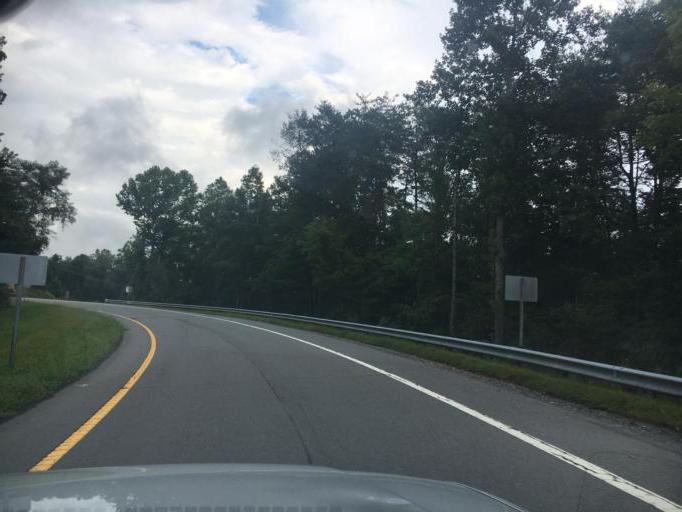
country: US
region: North Carolina
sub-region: McDowell County
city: West Marion
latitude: 35.6328
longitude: -82.0020
